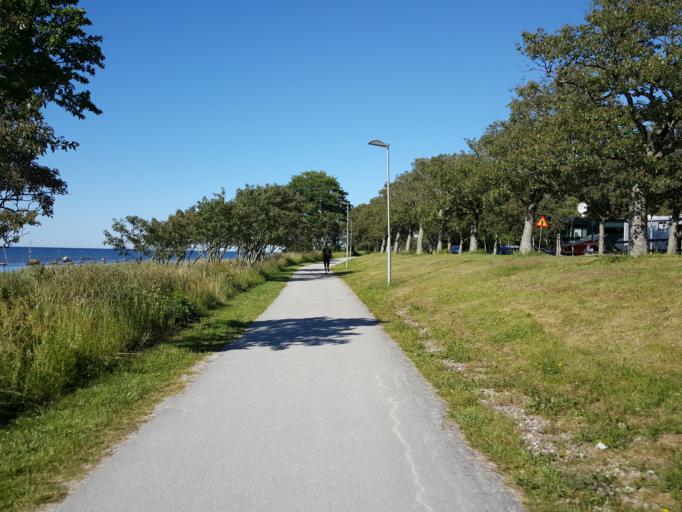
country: SE
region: Gotland
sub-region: Gotland
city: Visby
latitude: 57.6571
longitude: 18.3090
